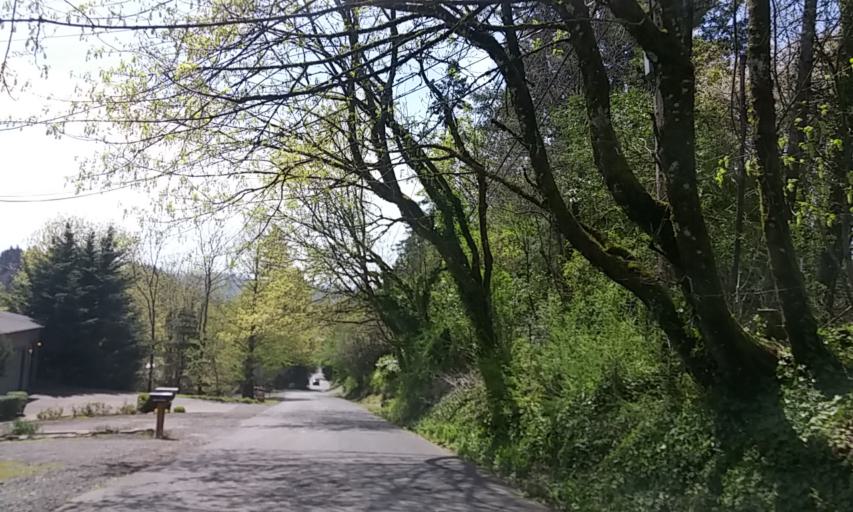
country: US
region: Oregon
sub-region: Washington County
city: West Haven-Sylvan
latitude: 45.5144
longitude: -122.7372
